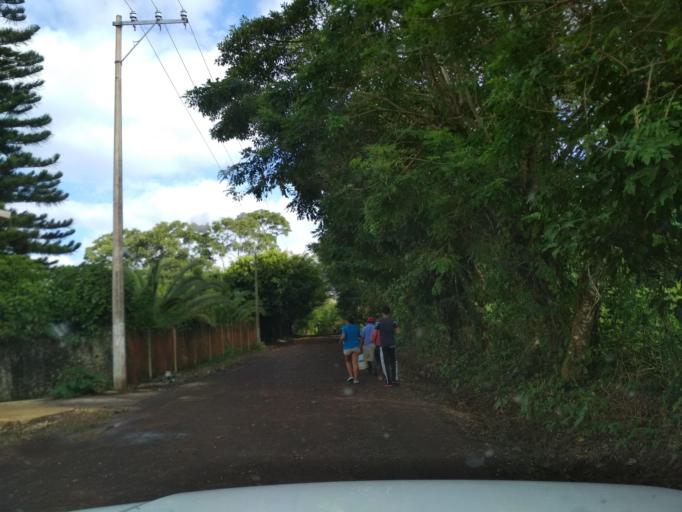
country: MX
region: Veracruz
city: Catemaco
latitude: 18.3714
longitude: -95.1140
